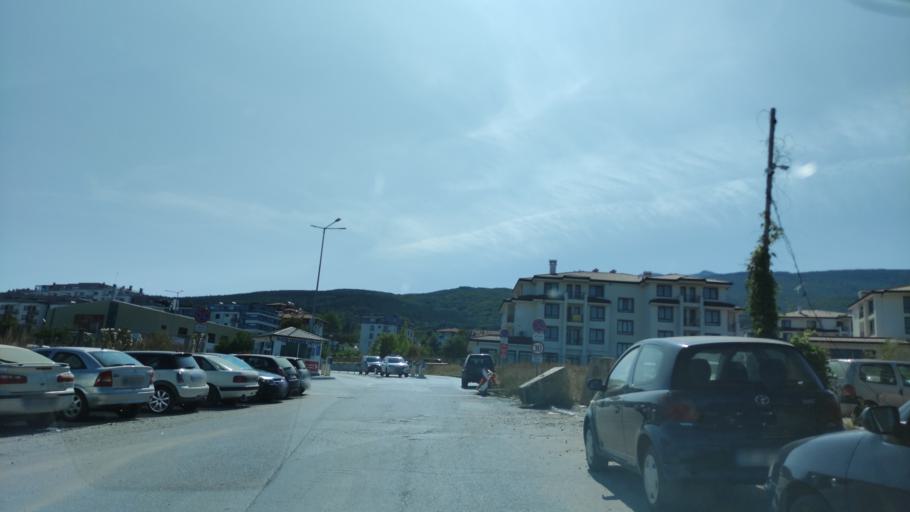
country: BG
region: Sofia-Capital
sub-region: Stolichna Obshtina
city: Sofia
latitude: 42.6184
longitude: 23.3486
